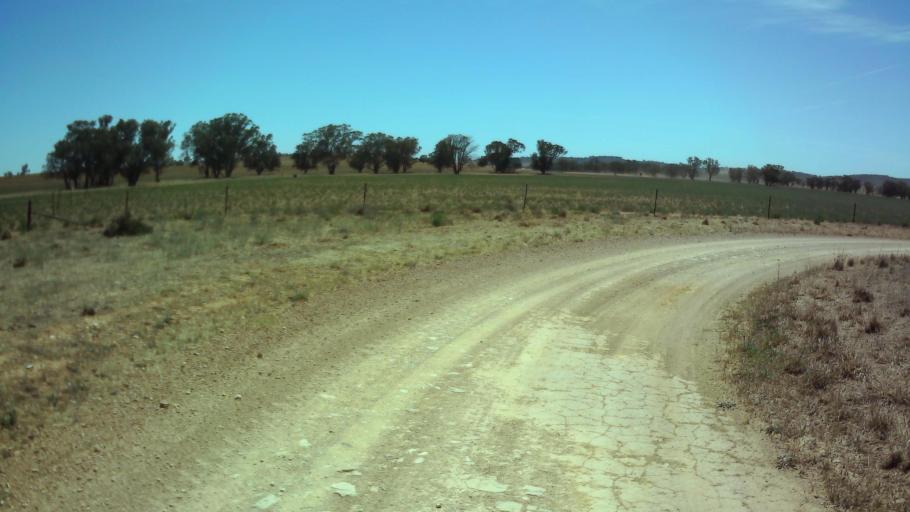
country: AU
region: New South Wales
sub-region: Weddin
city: Grenfell
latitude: -33.9923
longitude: 148.1572
